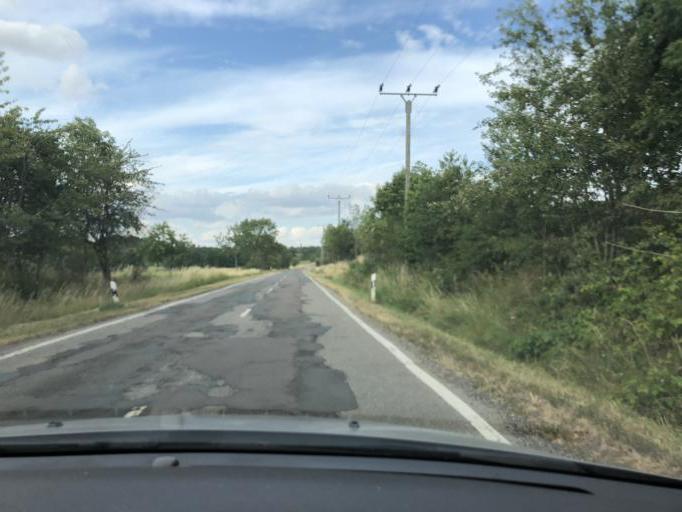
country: DE
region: Saxony-Anhalt
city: Osterfeld
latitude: 51.0655
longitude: 11.9007
